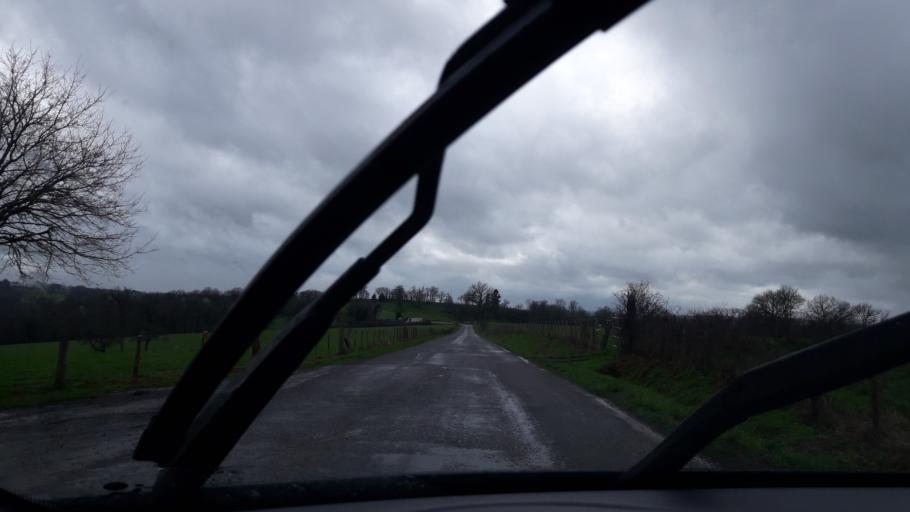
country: FR
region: Limousin
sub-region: Departement de la Haute-Vienne
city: Saint-Paul
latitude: 45.7429
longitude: 1.3994
